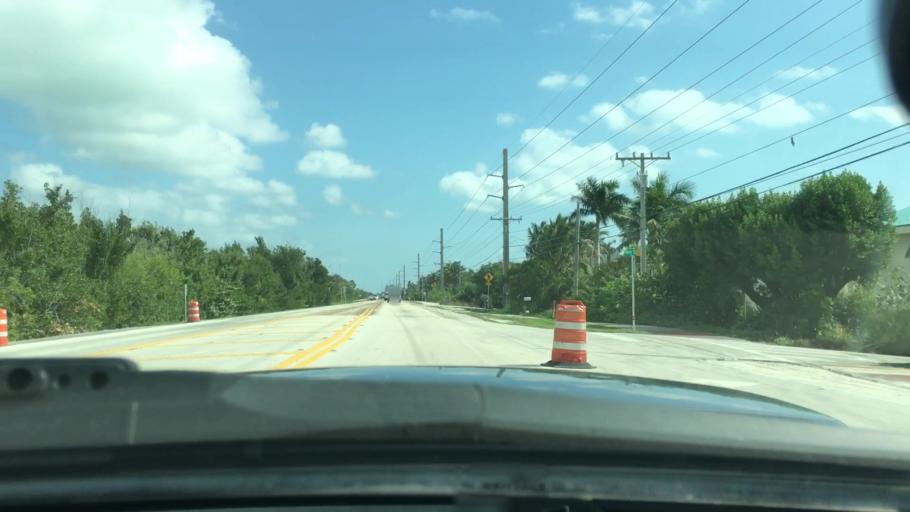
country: US
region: Florida
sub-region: Monroe County
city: Cudjoe Key
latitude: 24.6623
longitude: -81.4599
